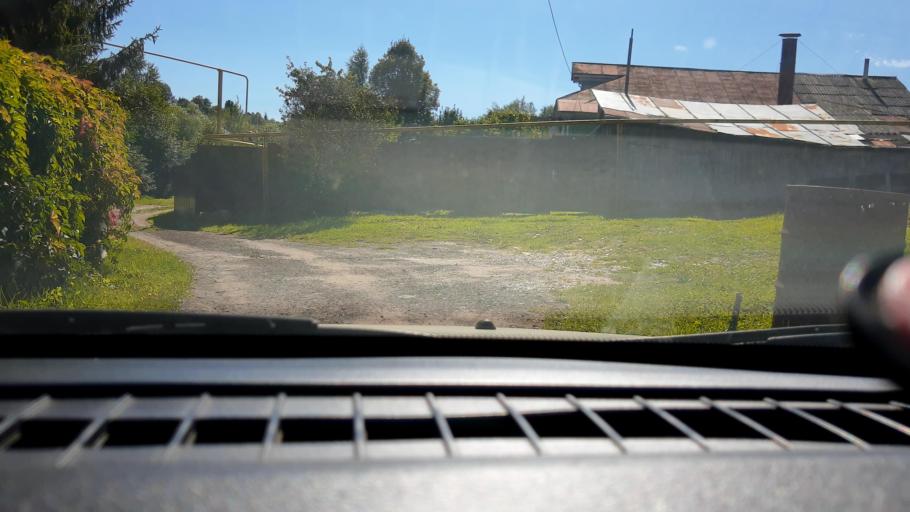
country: RU
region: Nizjnij Novgorod
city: Afonino
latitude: 56.2292
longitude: 44.0452
